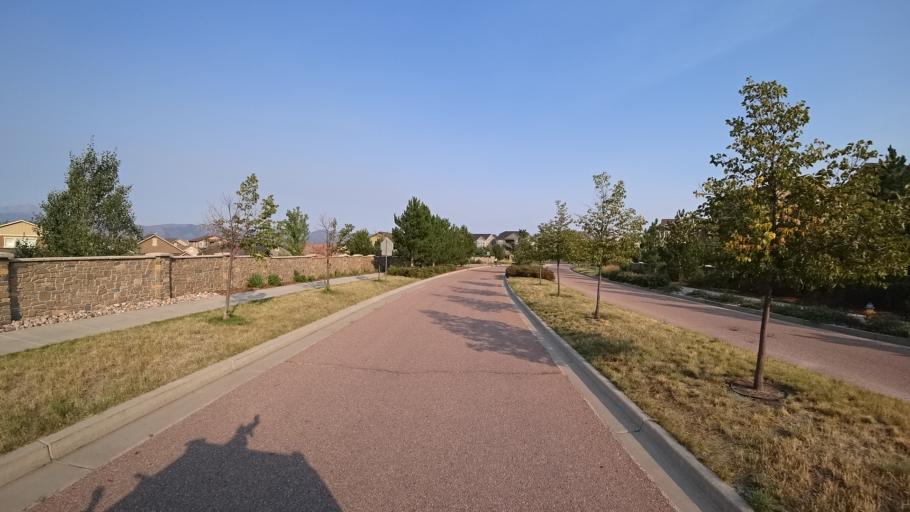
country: US
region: Colorado
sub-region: El Paso County
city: Black Forest
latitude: 38.9760
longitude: -104.7376
